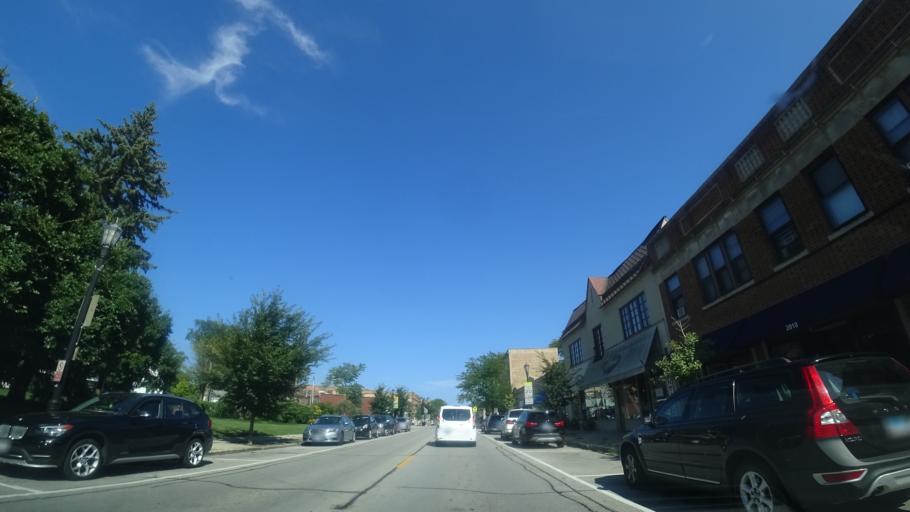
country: US
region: Illinois
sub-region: Cook County
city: Wilmette
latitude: 42.0644
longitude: -87.7019
